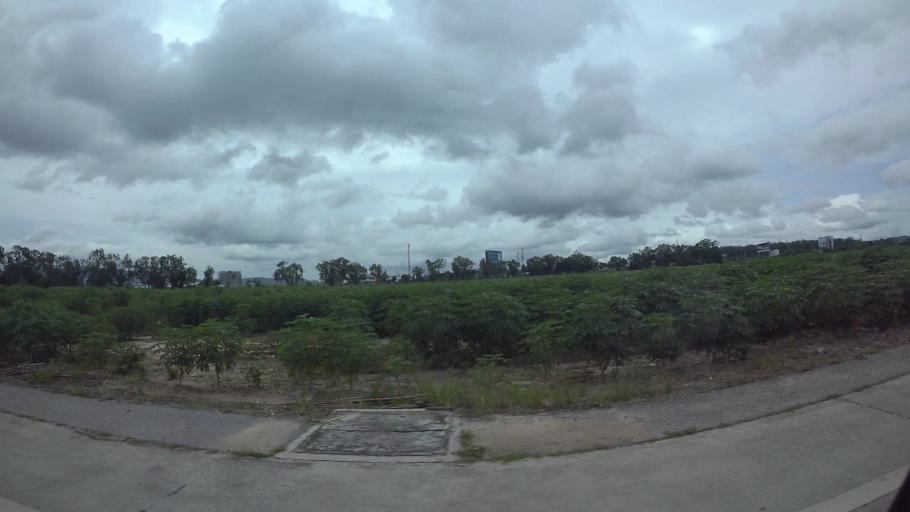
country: TH
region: Chon Buri
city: Si Racha
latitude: 13.1671
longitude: 100.9864
